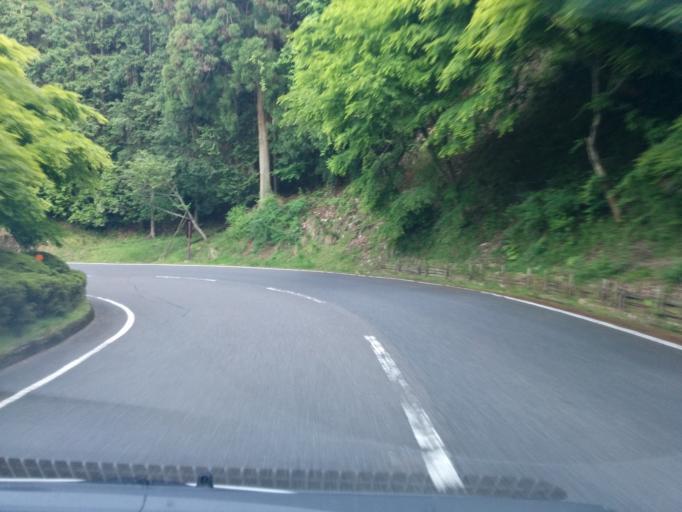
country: JP
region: Shiga Prefecture
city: Kitahama
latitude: 35.1045
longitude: 135.8585
